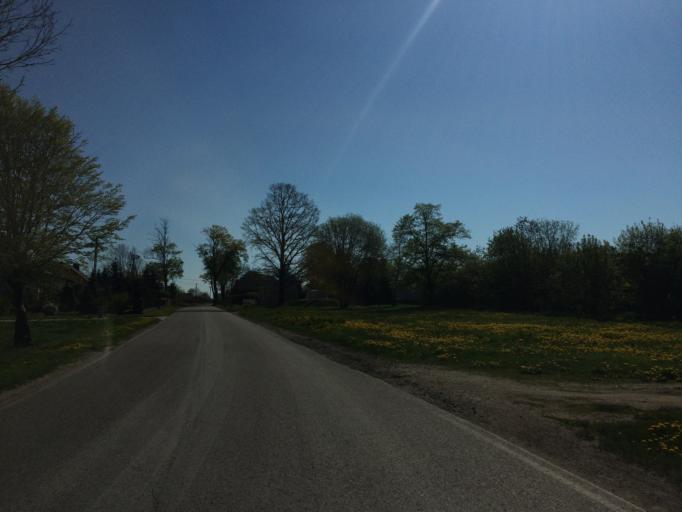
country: PL
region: Warmian-Masurian Voivodeship
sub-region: Powiat ostrodzki
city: Dabrowno
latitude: 53.5048
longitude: 19.9984
